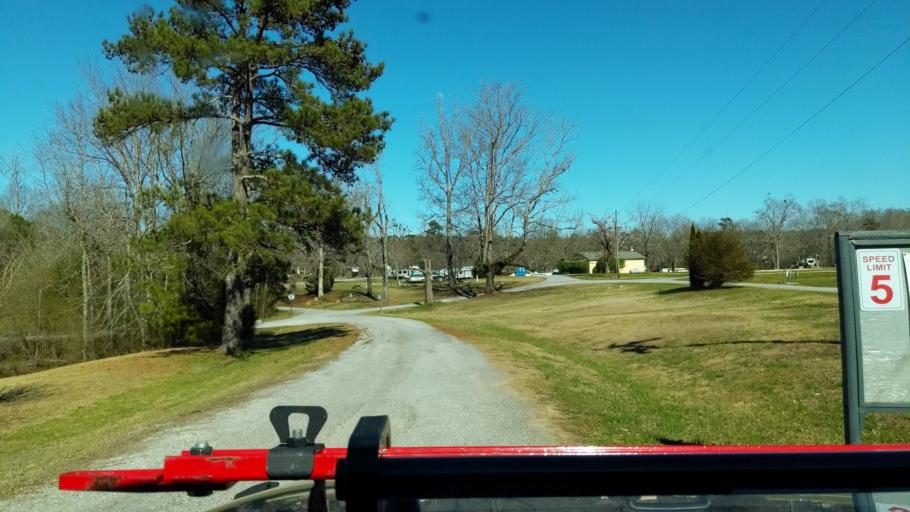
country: US
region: Alabama
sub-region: Walker County
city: Jasper
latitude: 34.0541
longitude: -87.1461
